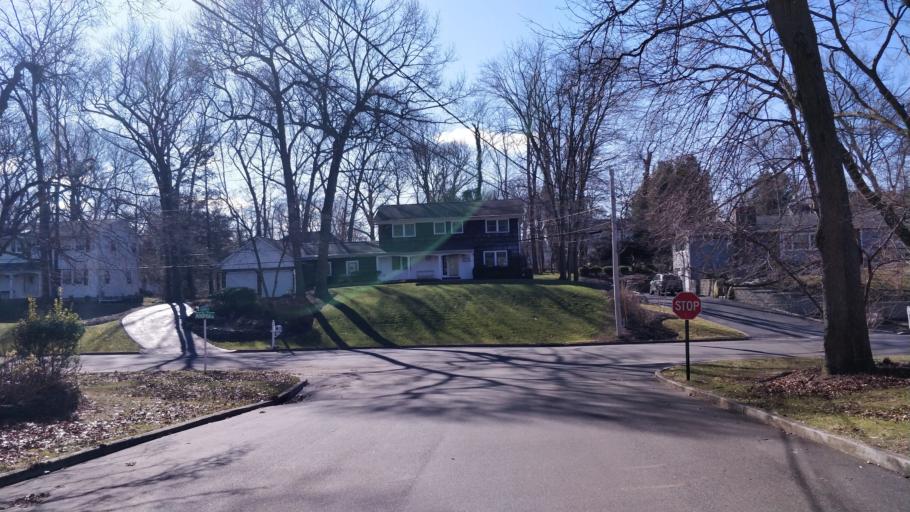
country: US
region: New York
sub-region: Suffolk County
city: Setauket-East Setauket
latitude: 40.9276
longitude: -73.1093
